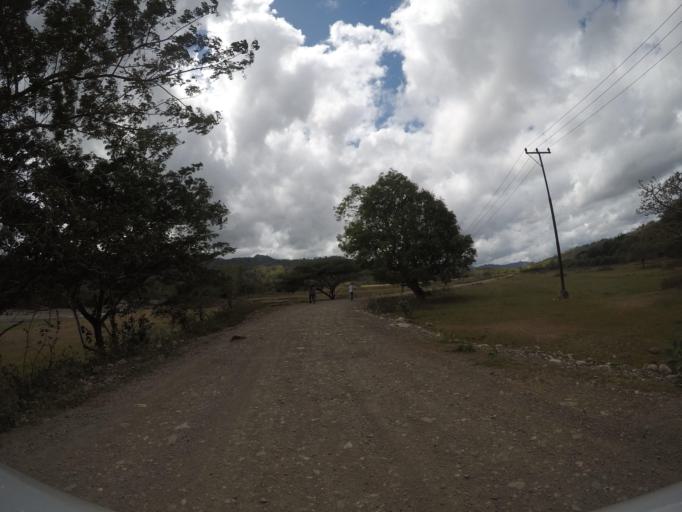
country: TL
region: Lautem
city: Lospalos
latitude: -8.4886
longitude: 126.8205
